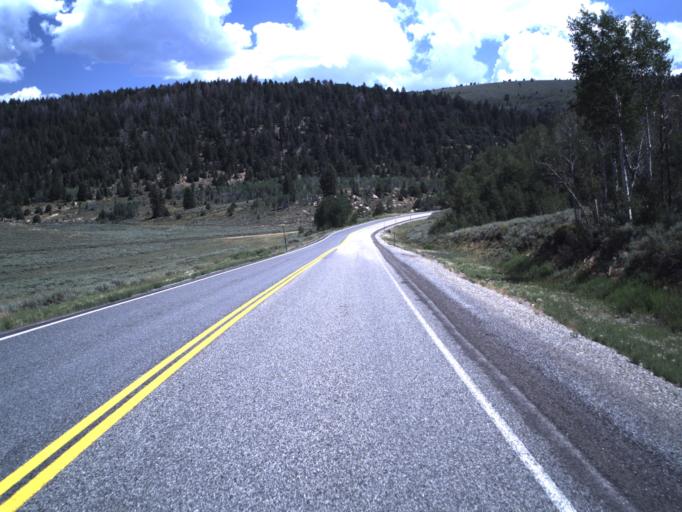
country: US
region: Utah
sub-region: Carbon County
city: Helper
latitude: 39.8624
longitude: -111.1231
